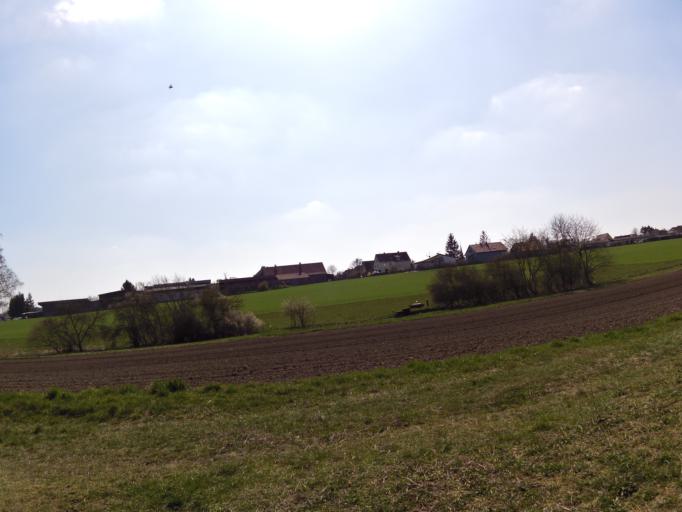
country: DE
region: Bavaria
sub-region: Regierungsbezirk Unterfranken
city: Biebelried
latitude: 49.7341
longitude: 10.0905
